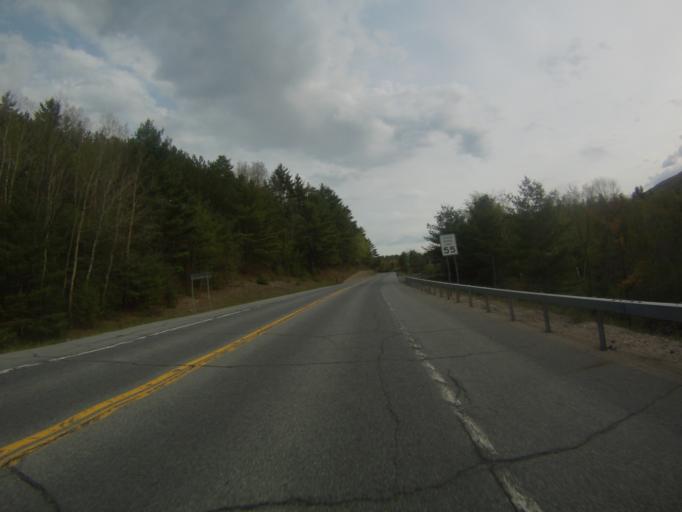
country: US
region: New York
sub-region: Warren County
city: Warrensburg
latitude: 43.6936
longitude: -73.9874
